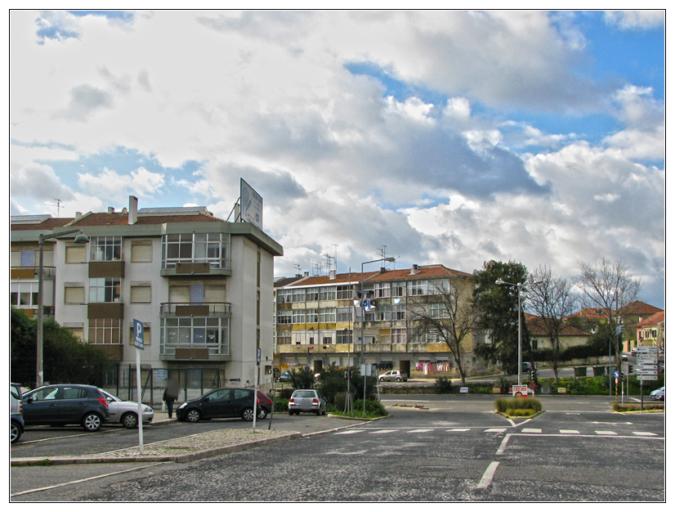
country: PT
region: Lisbon
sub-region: Sintra
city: Rio de Mouro
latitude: 38.7968
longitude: -9.3361
